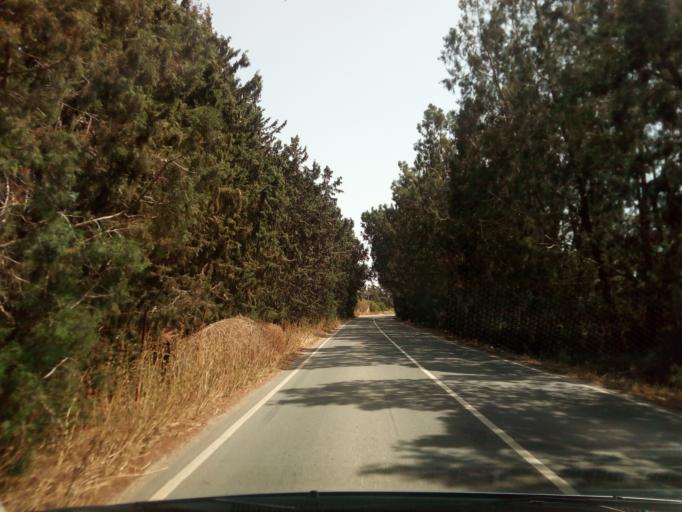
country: CY
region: Larnaka
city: Meneou
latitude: 34.8554
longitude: 33.5956
